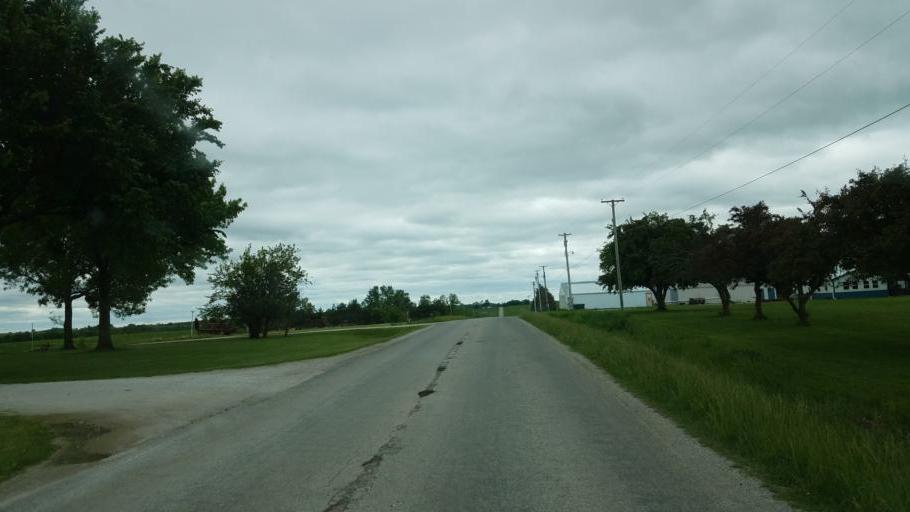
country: US
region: Iowa
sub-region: Decatur County
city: Lamoni
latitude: 40.6108
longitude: -93.9200
